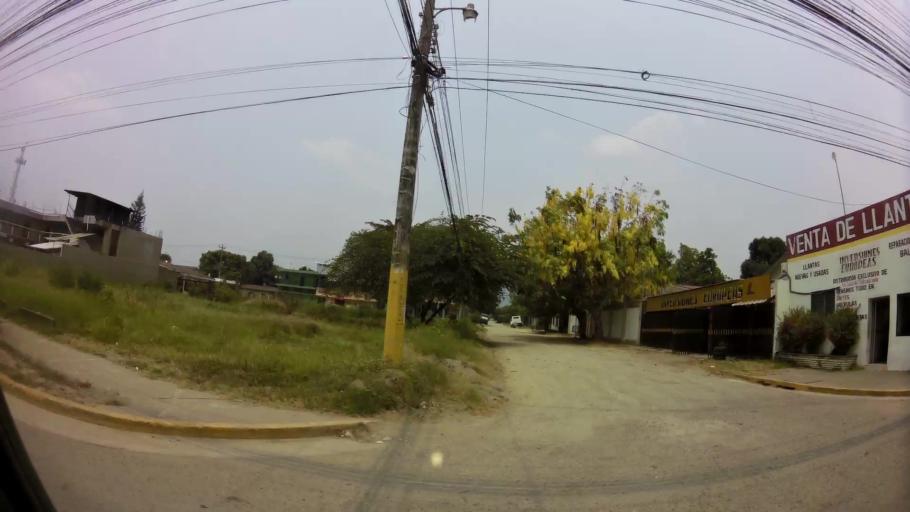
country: HN
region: Yoro
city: El Progreso
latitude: 15.3974
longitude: -87.8089
